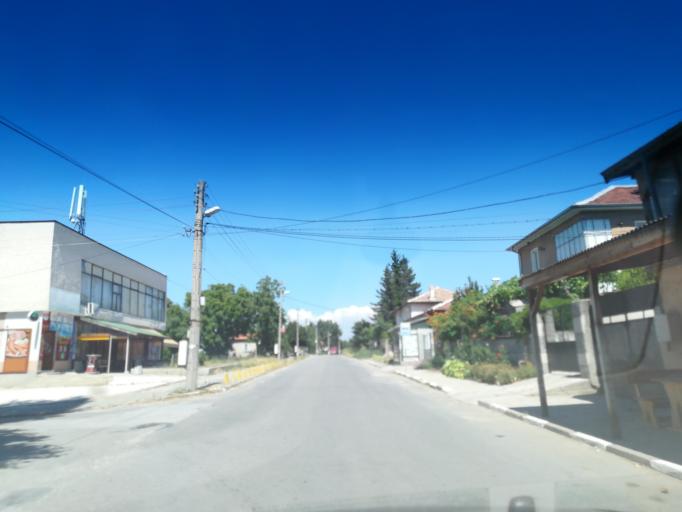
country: BG
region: Plovdiv
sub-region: Obshtina Asenovgrad
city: Asenovgrad
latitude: 42.0205
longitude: 24.9705
